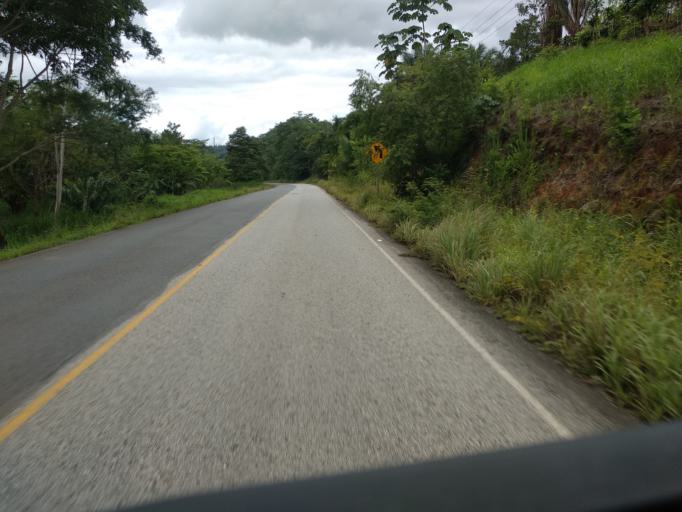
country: CR
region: Puntarenas
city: Buenos Aires
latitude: 9.1082
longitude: -83.2863
